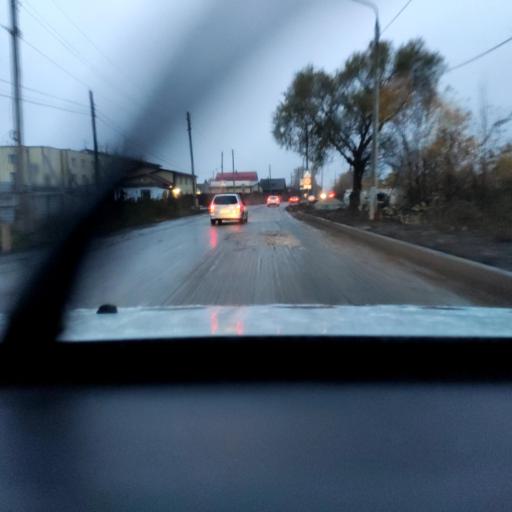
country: RU
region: Perm
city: Kondratovo
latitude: 57.9619
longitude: 56.1236
